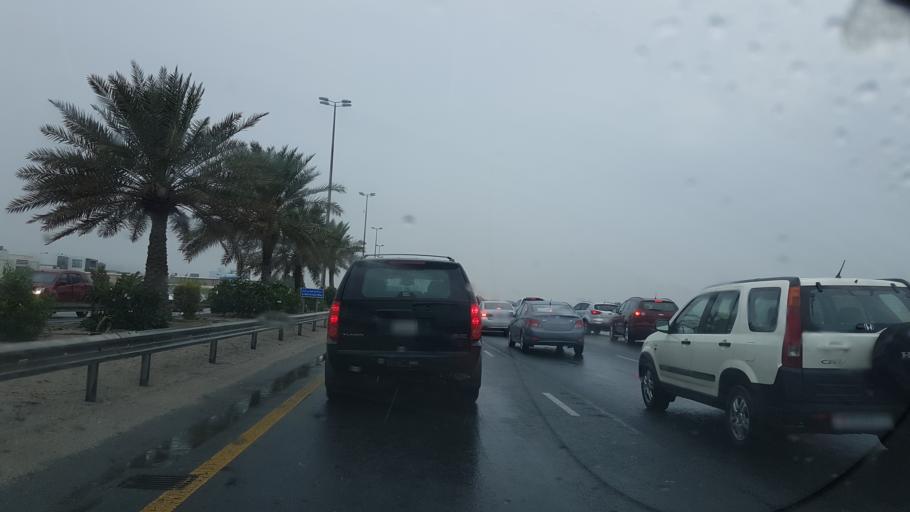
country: BH
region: Manama
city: Jidd Hafs
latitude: 26.1979
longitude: 50.5088
